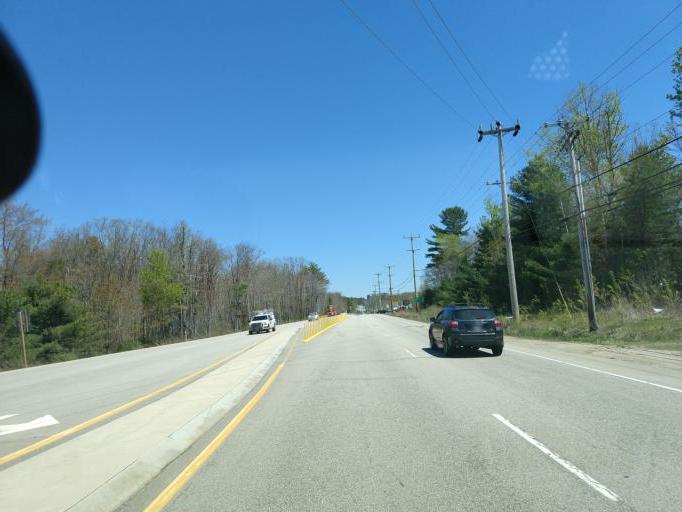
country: US
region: Maine
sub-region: York County
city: York Harbor
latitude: 43.1553
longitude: -70.6578
